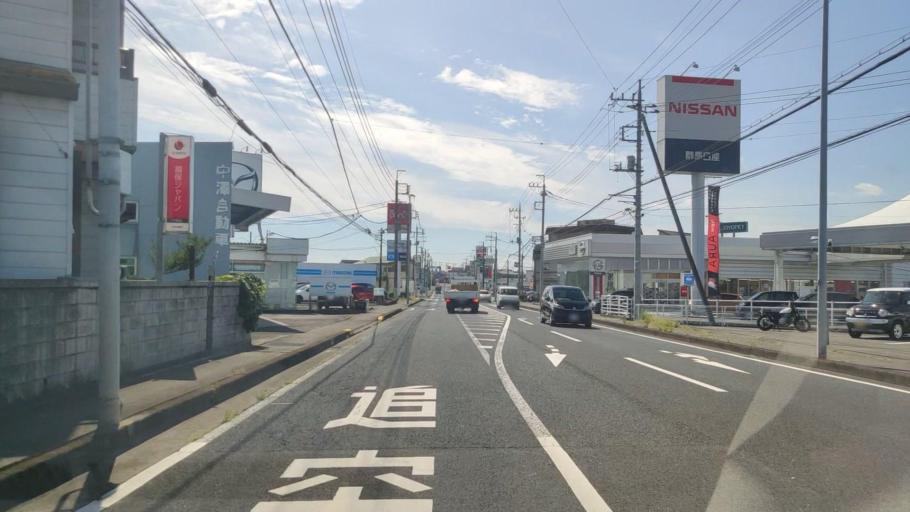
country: JP
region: Gunma
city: Shibukawa
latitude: 36.5109
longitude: 139.0053
